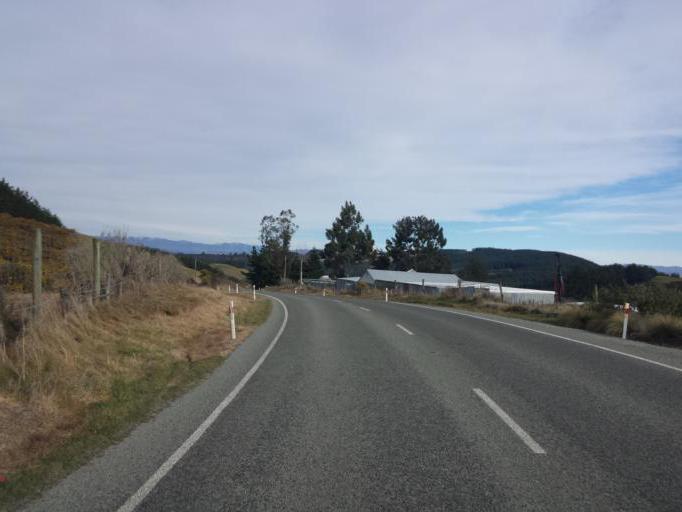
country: NZ
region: Canterbury
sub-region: Timaru District
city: Pleasant Point
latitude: -44.1232
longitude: 171.1052
